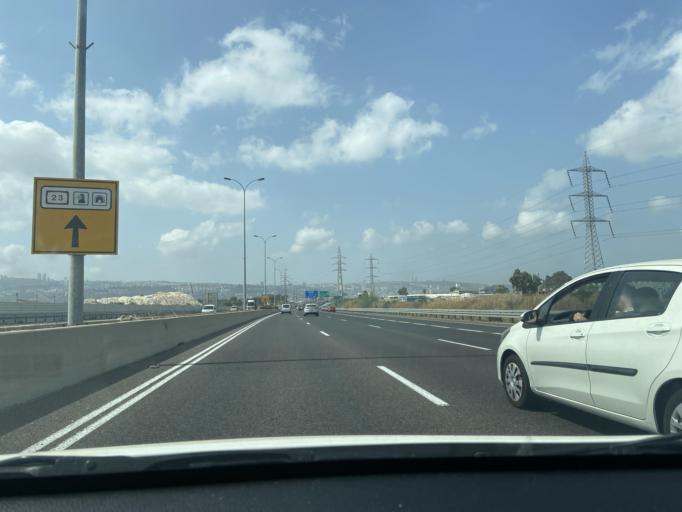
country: IL
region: Haifa
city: Qiryat Bialik
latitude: 32.8060
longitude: 35.0653
